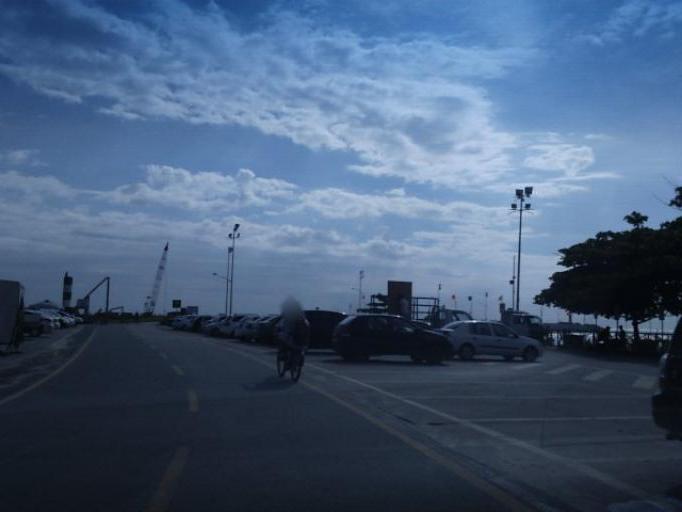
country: BR
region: Santa Catarina
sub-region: Navegantes
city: Navegantes
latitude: -26.9150
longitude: -48.6420
